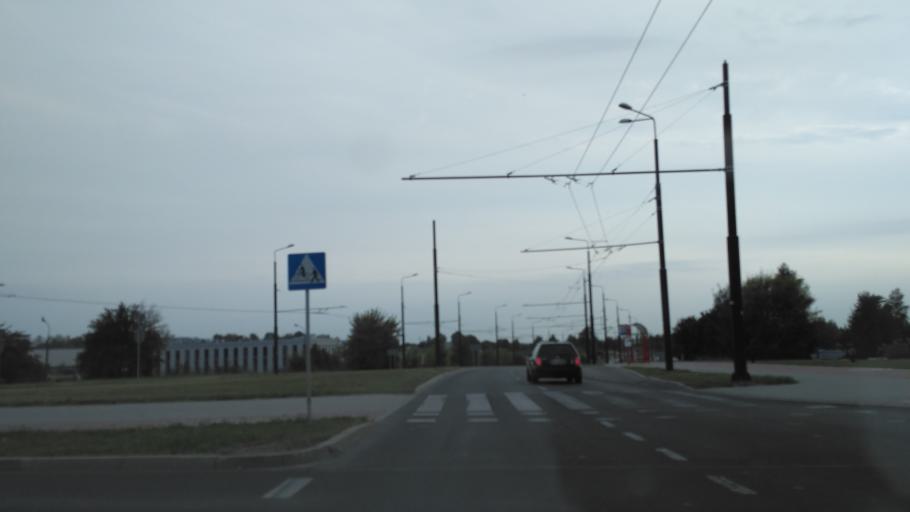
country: PL
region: Lublin Voivodeship
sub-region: Powiat lubelski
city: Jakubowice Murowane
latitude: 51.2280
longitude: 22.6187
